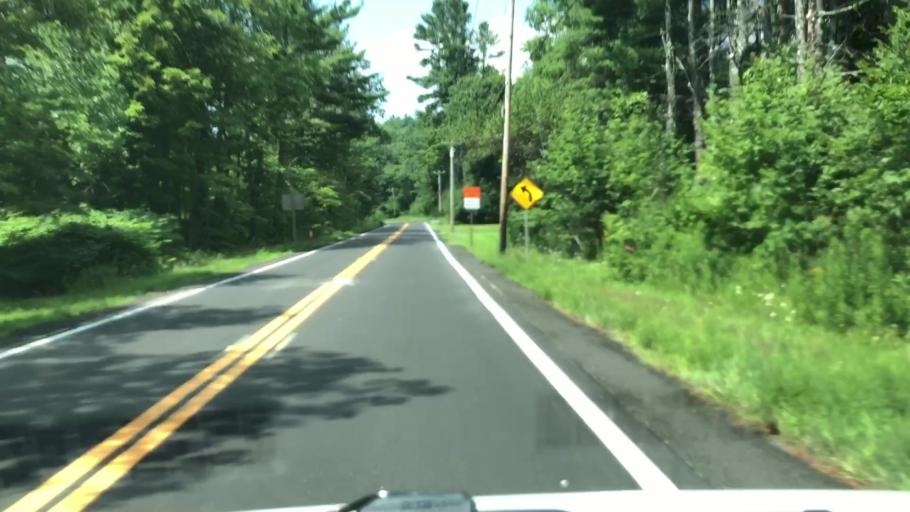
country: US
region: Massachusetts
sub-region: Franklin County
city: Ashfield
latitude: 42.5174
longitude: -72.7474
